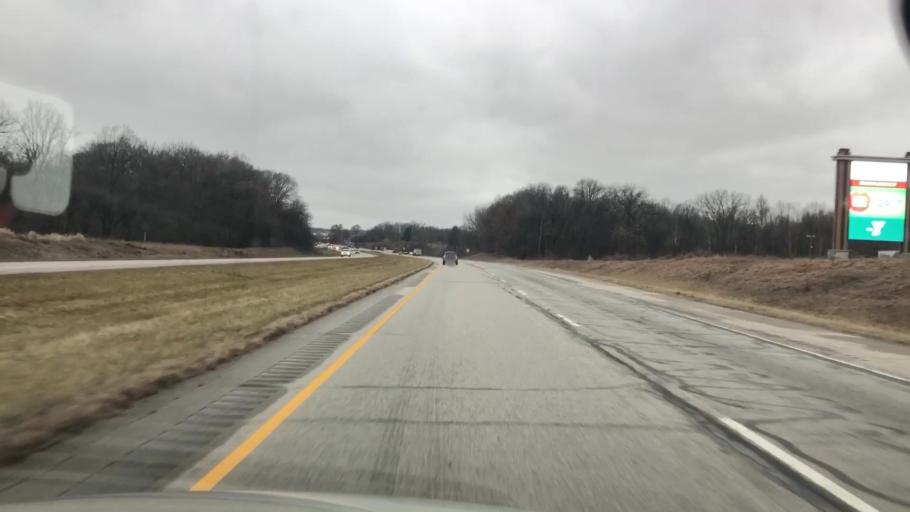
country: US
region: Indiana
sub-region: Kosciusko County
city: Warsaw
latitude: 41.2566
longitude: -85.8316
